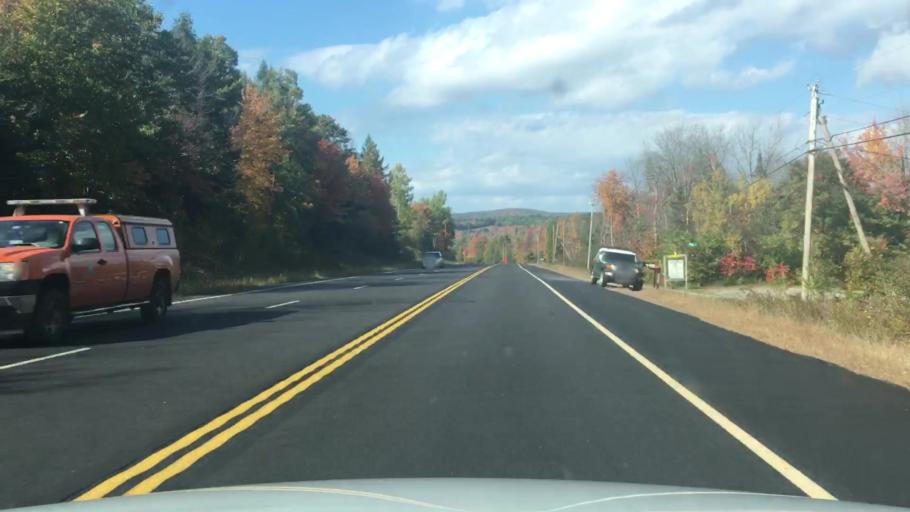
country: US
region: Maine
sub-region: Waldo County
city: Palermo
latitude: 44.3753
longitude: -69.3960
